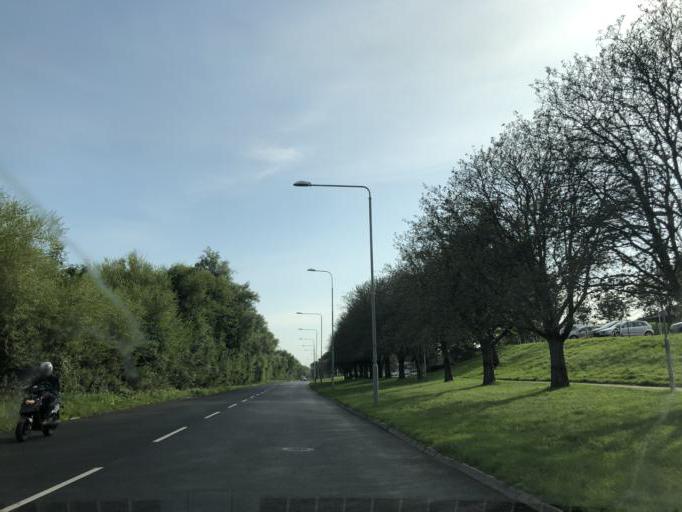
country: SE
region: Vaestra Goetaland
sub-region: Goteborg
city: Goeteborg
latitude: 57.7449
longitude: 11.9883
